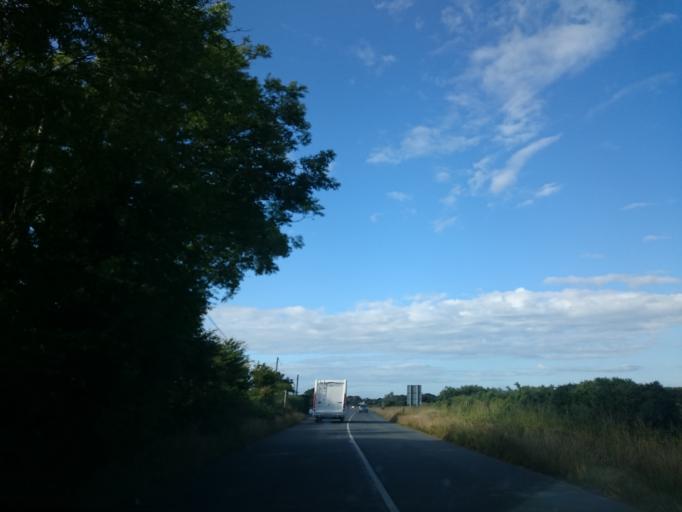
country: IE
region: Leinster
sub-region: Loch Garman
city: Loch Garman
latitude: 52.2253
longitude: -6.5063
